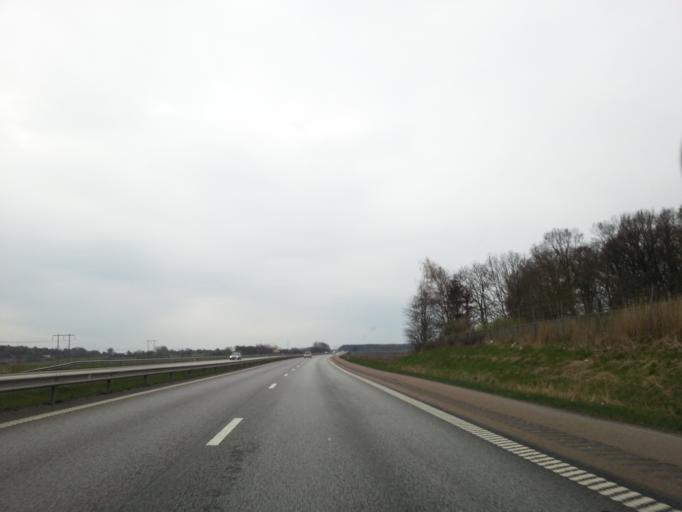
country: SE
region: Halland
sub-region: Varbergs Kommun
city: Traslovslage
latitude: 57.1105
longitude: 12.3324
